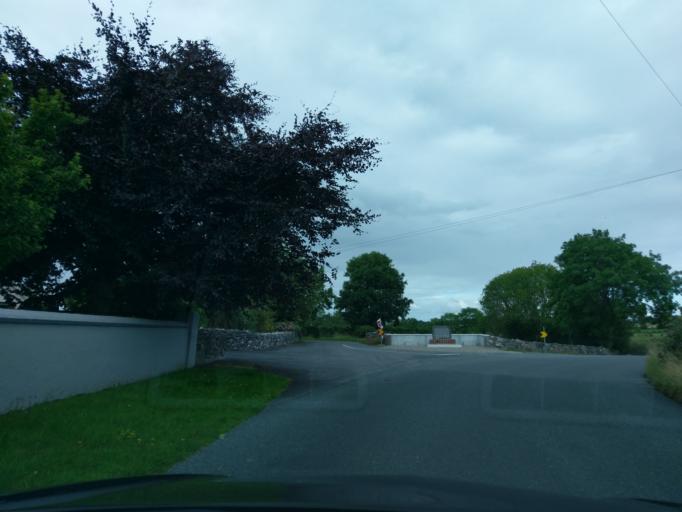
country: IE
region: Connaught
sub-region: County Galway
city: Gort
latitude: 53.1659
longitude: -8.7773
